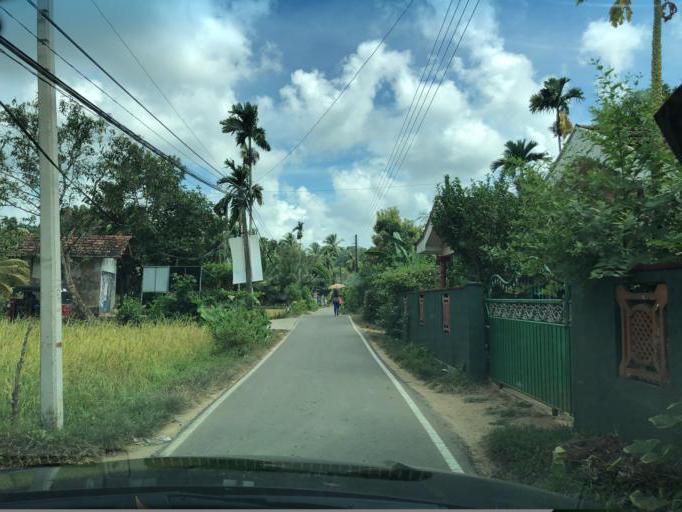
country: LK
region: Western
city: Horawala Junction
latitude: 6.5307
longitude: 80.0983
